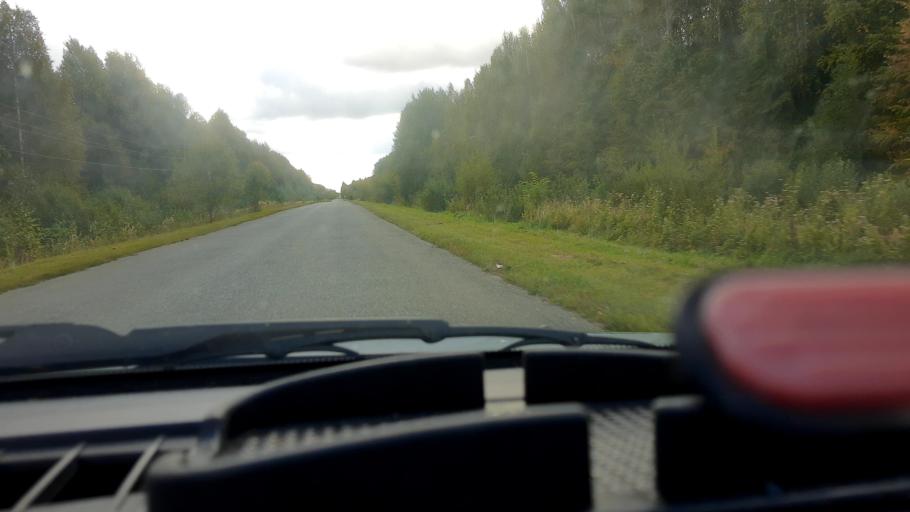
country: RU
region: Mariy-El
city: Kilemary
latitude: 56.9145
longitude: 46.7243
